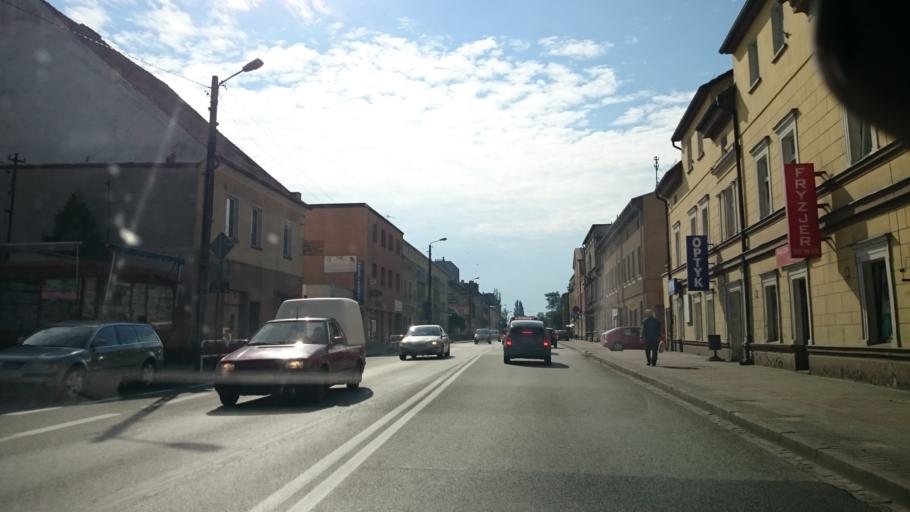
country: PL
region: Opole Voivodeship
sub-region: Powiat strzelecki
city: Strzelce Opolskie
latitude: 50.5089
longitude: 18.3056
